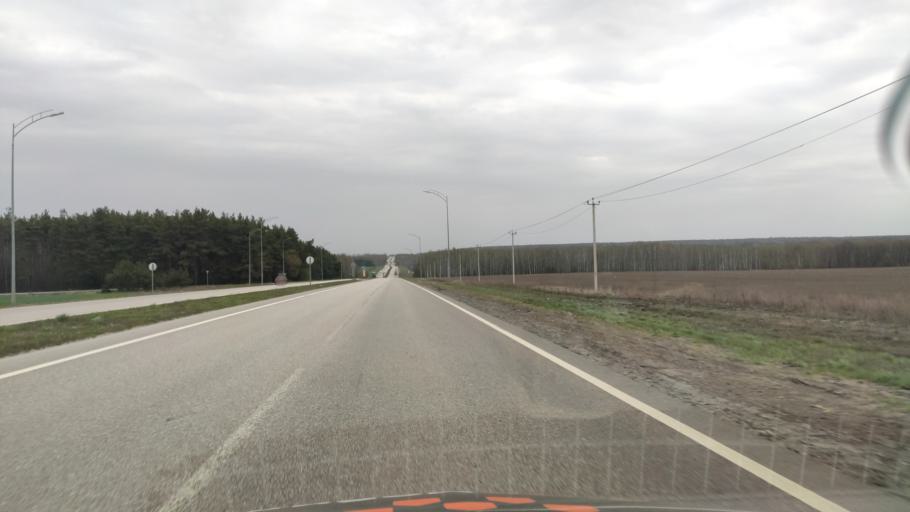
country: RU
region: Belgorod
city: Staryy Oskol
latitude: 51.3975
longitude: 37.8734
